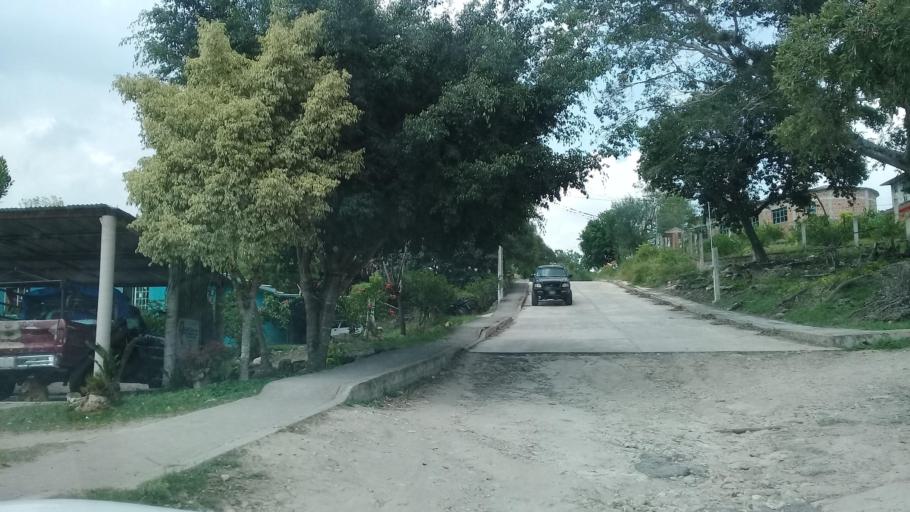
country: MX
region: Veracruz
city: Jalcomulco
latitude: 19.3894
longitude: -96.7928
